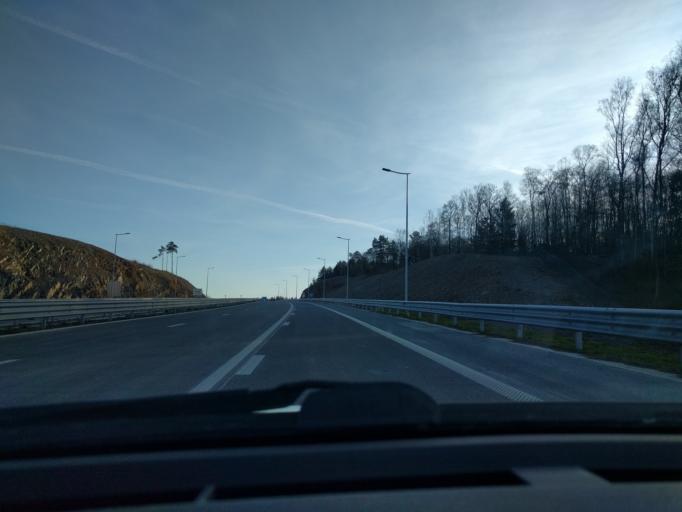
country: BE
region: Wallonia
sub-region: Province de Namur
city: Couvin
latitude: 50.0663
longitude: 4.5047
